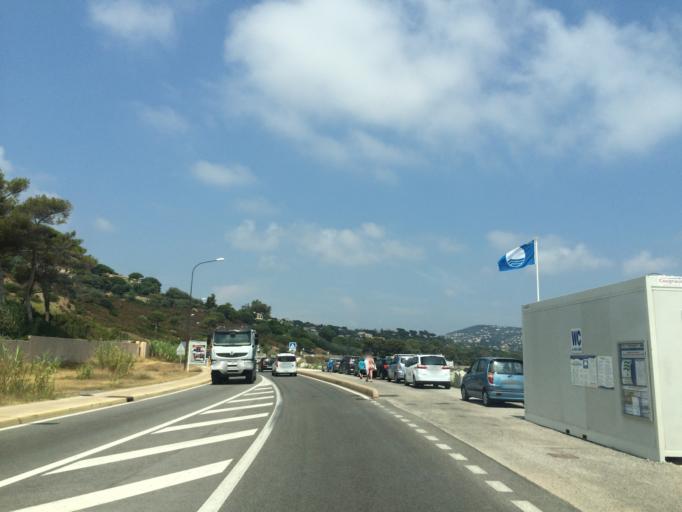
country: FR
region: Provence-Alpes-Cote d'Azur
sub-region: Departement du Var
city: Sainte-Maxime
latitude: 43.3309
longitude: 6.6684
